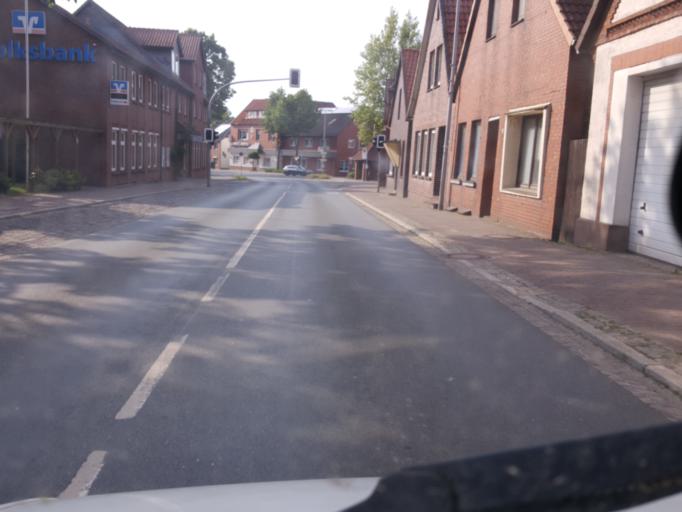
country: DE
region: Lower Saxony
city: Liebenau
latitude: 52.6034
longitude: 9.0971
